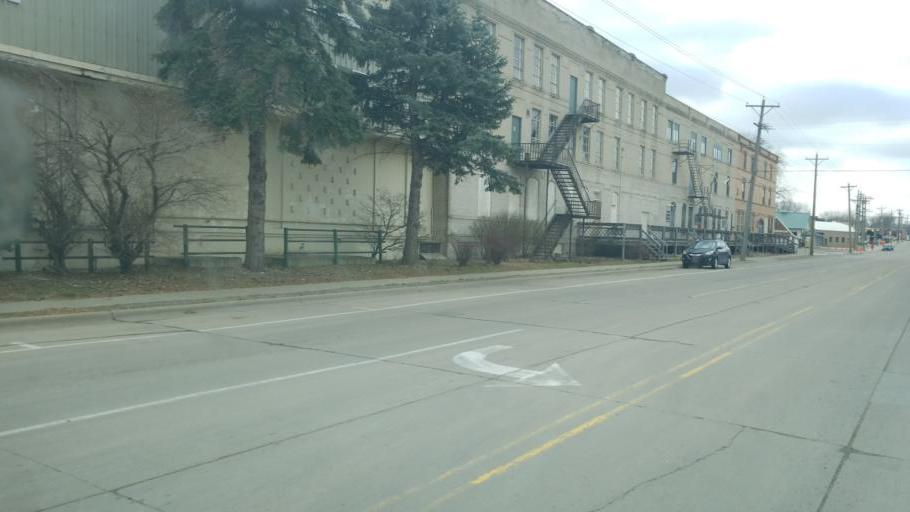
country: US
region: South Dakota
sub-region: Yankton County
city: Yankton
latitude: 42.8685
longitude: -97.3892
